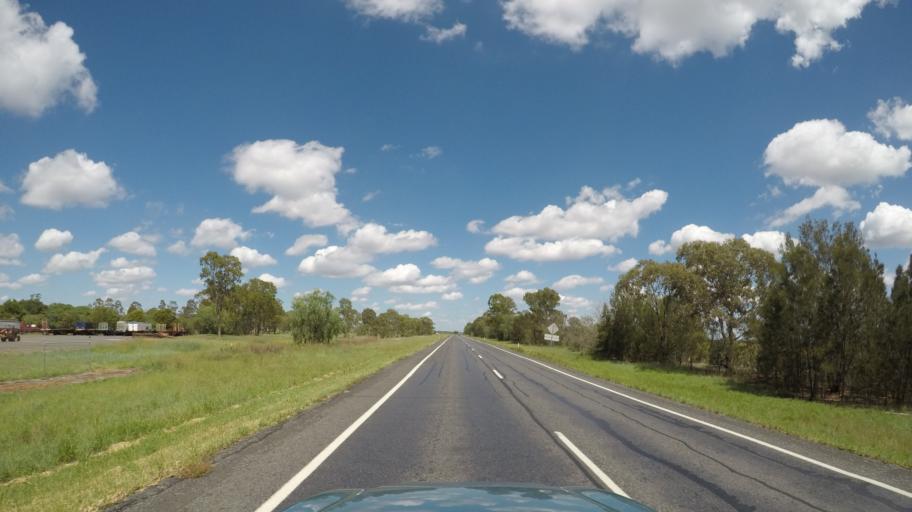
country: AU
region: Queensland
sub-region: Toowoomba
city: Oakey
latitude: -27.7553
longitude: 151.4530
